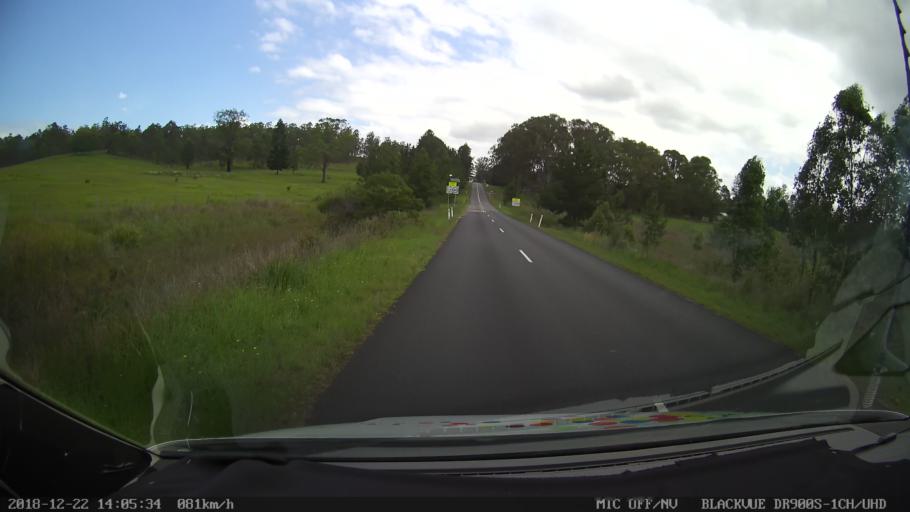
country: AU
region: New South Wales
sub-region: Clarence Valley
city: Coutts Crossing
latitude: -29.9461
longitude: 152.7296
